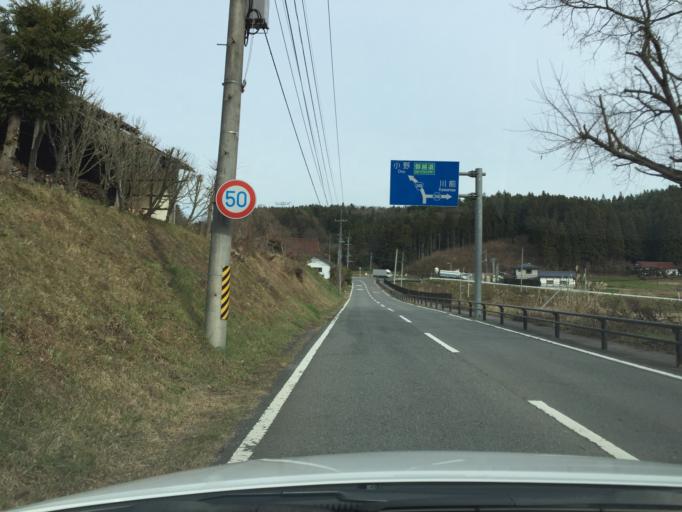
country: JP
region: Fukushima
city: Ishikawa
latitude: 37.1953
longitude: 140.6268
